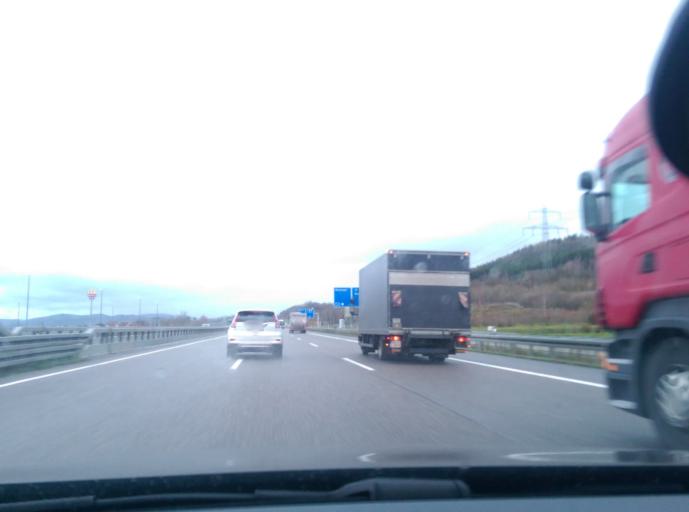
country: DE
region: Hesse
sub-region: Regierungsbezirk Kassel
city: Herleshausen
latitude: 51.0070
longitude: 10.1840
